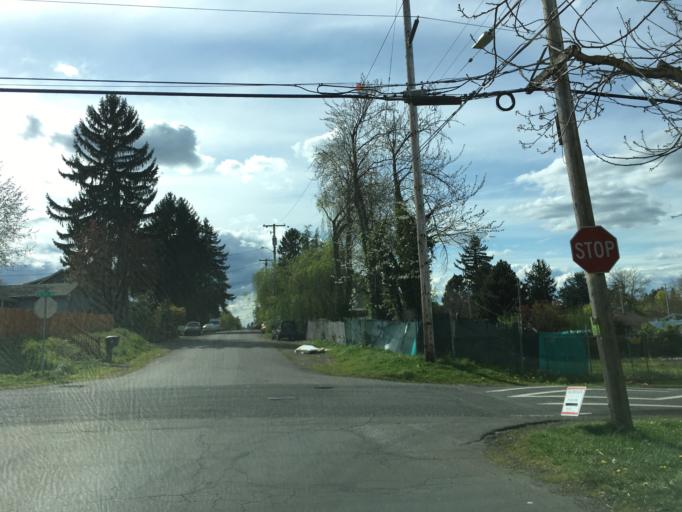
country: US
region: Oregon
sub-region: Multnomah County
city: Lents
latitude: 45.5572
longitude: -122.5472
